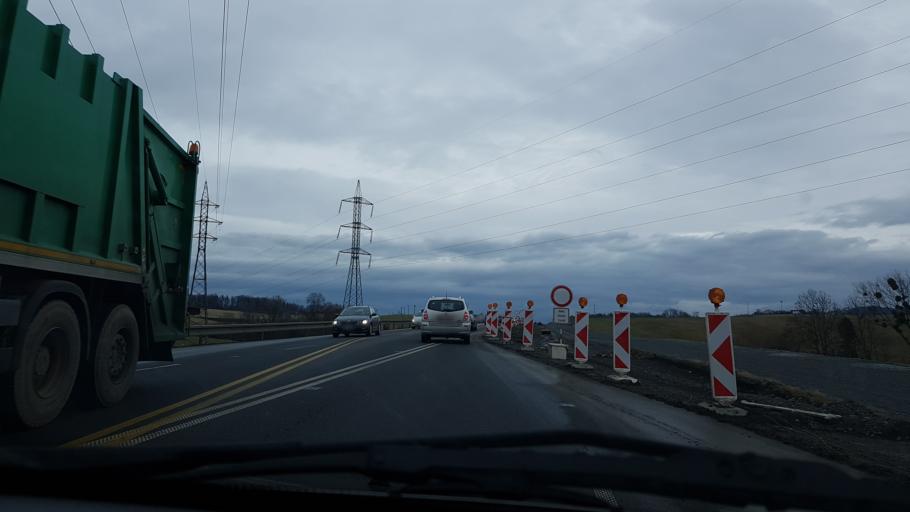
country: CZ
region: Moravskoslezsky
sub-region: Okres Novy Jicin
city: Pribor
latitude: 49.6433
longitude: 18.1712
